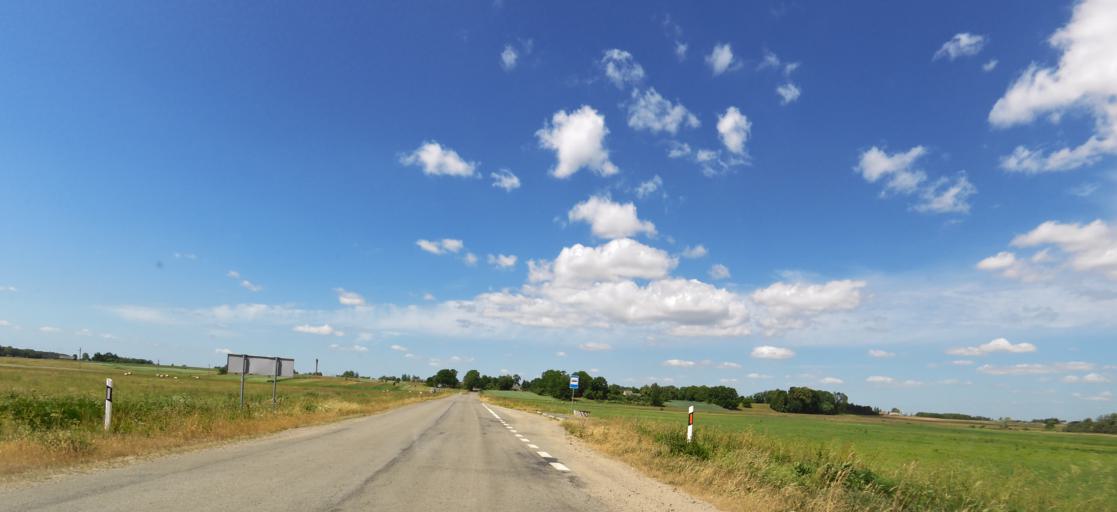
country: LT
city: Kupiskis
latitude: 55.9339
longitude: 24.8936
